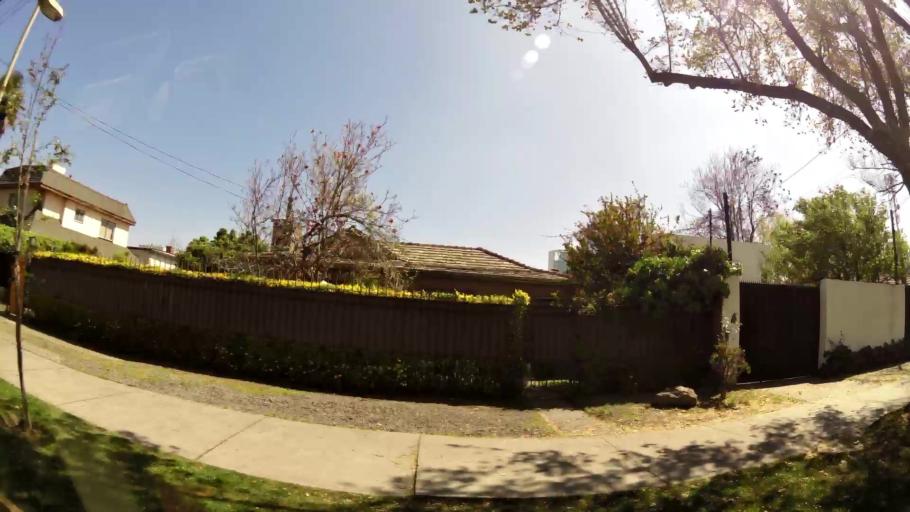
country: CL
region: Santiago Metropolitan
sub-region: Provincia de Santiago
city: Villa Presidente Frei, Nunoa, Santiago, Chile
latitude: -33.4096
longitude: -70.5568
